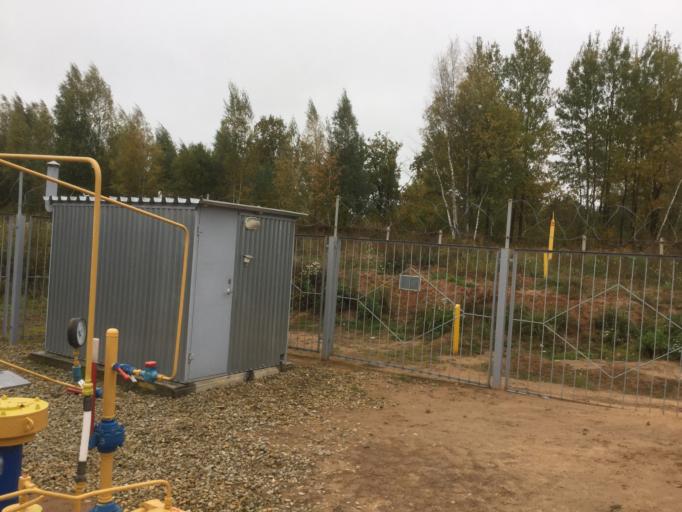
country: BY
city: Novolukoml'
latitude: 54.7346
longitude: 29.1318
